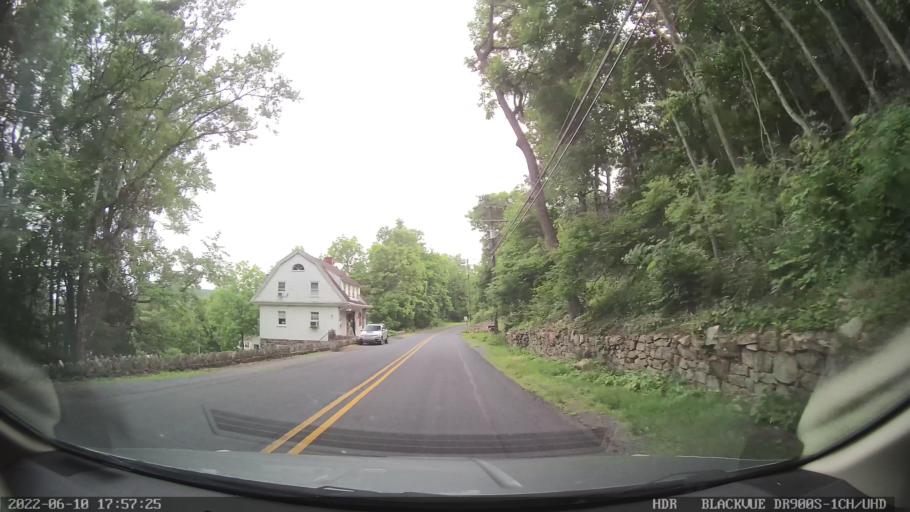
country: US
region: Pennsylvania
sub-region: Berks County
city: Pennside
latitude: 40.3415
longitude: -75.8802
